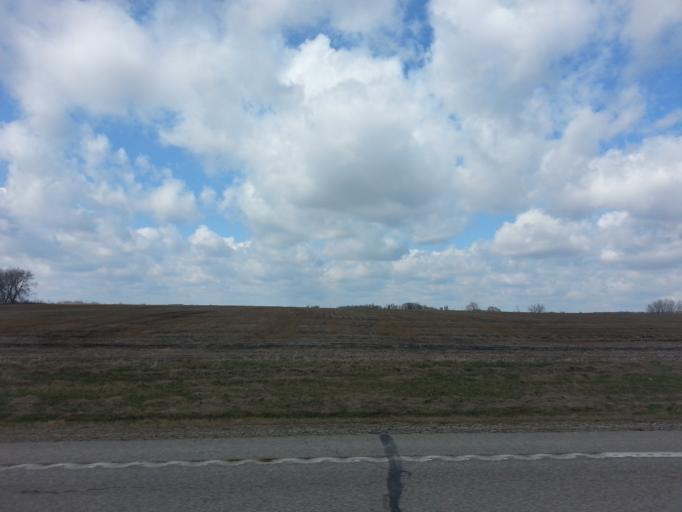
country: US
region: Minnesota
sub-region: Dodge County
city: Mantorville
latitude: 44.0800
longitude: -92.7671
